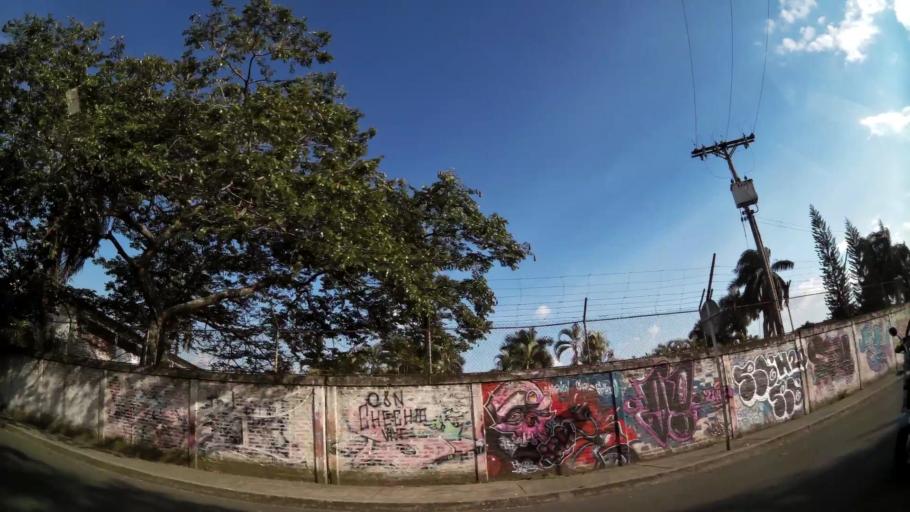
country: CO
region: Valle del Cauca
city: Cali
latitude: 3.4063
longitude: -76.4989
